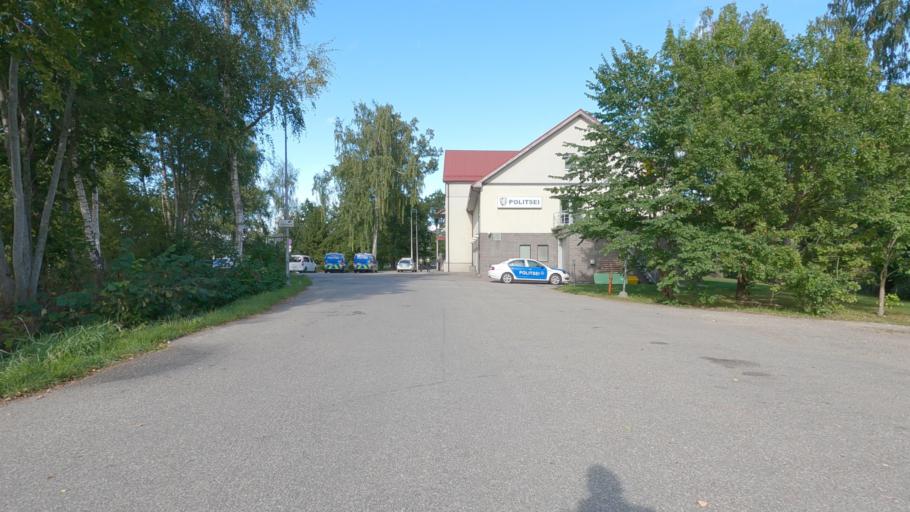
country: EE
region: Raplamaa
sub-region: Rapla vald
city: Rapla
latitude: 58.9942
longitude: 24.8255
